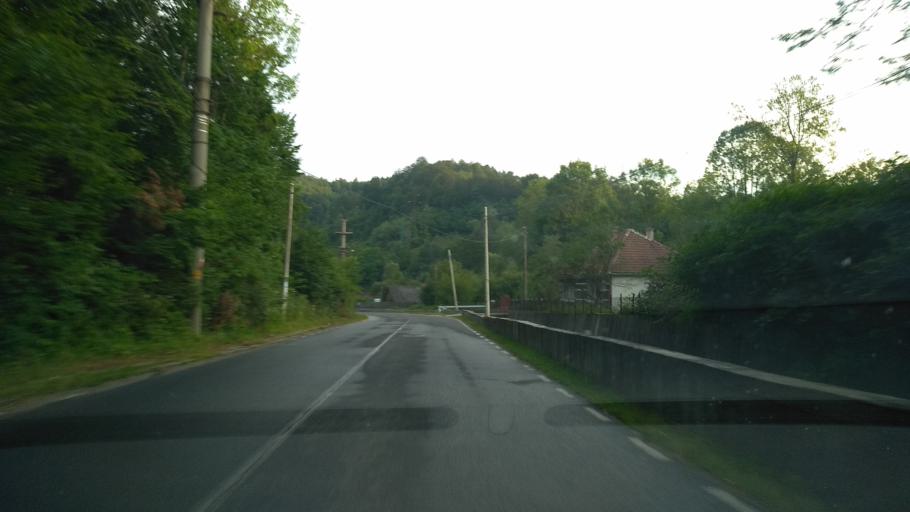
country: RO
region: Hunedoara
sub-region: Comuna Aninoasa
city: Aninoasa
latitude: 45.3949
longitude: 23.3184
